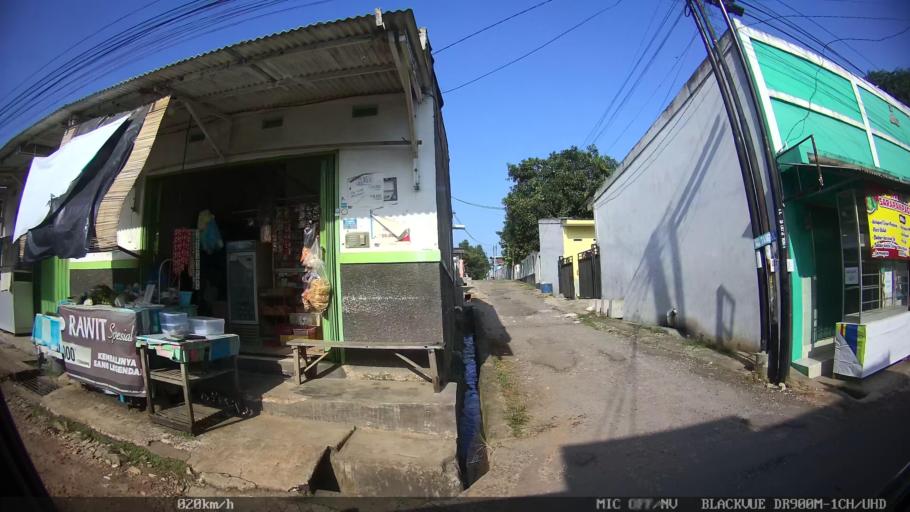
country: ID
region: Lampung
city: Kedaton
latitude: -5.3715
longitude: 105.2333
